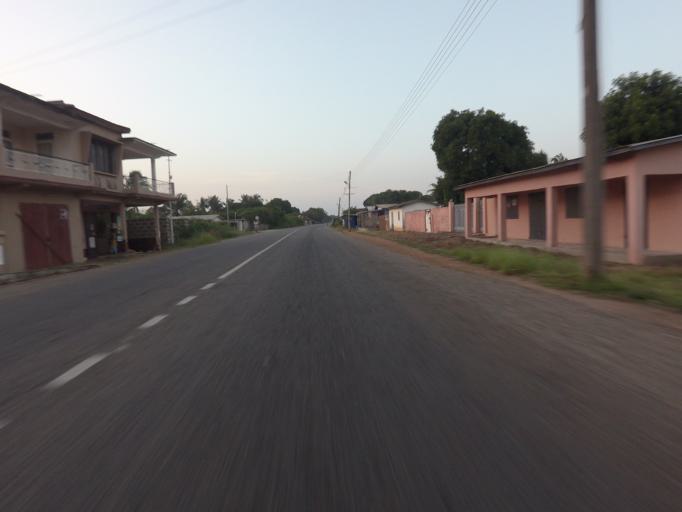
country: GH
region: Volta
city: Keta
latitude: 5.8685
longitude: 0.9790
